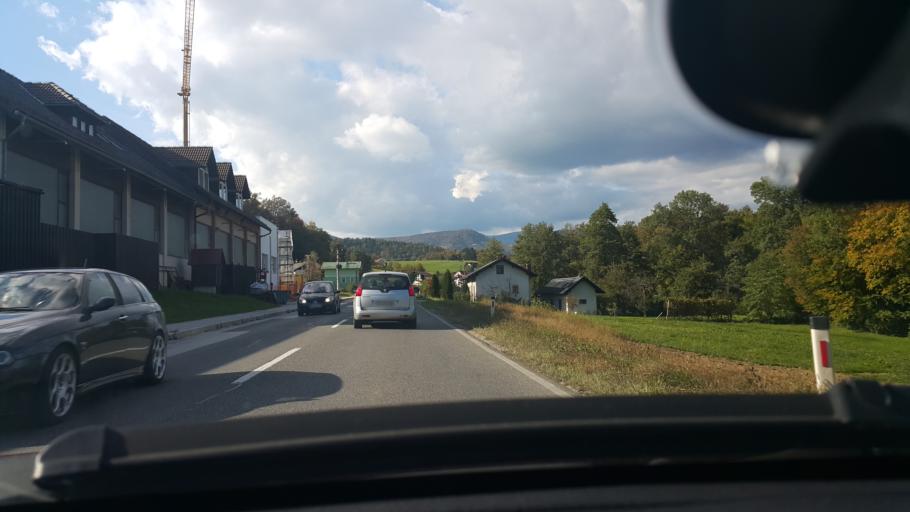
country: SI
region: Slovenska Konjice
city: Slovenske Konjice
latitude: 46.3485
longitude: 15.4048
